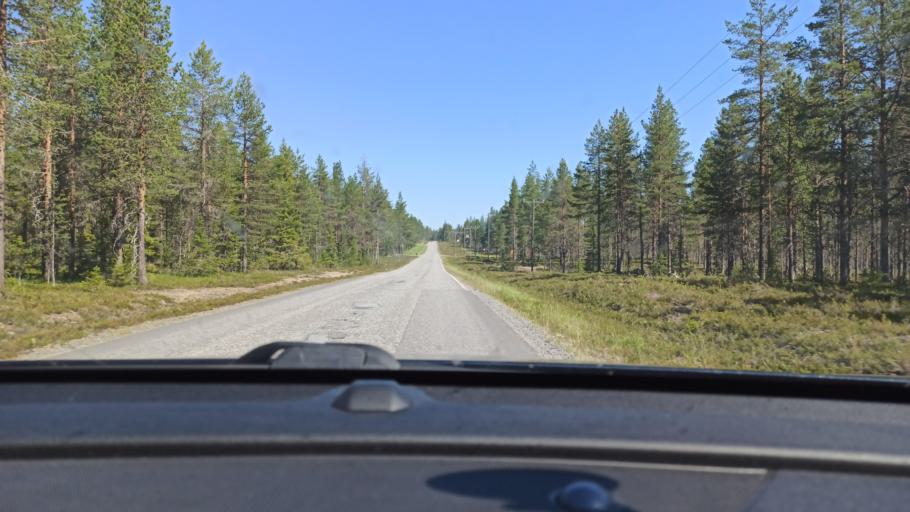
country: FI
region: Lapland
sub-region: Tunturi-Lappi
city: Kolari
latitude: 67.6505
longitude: 24.1620
